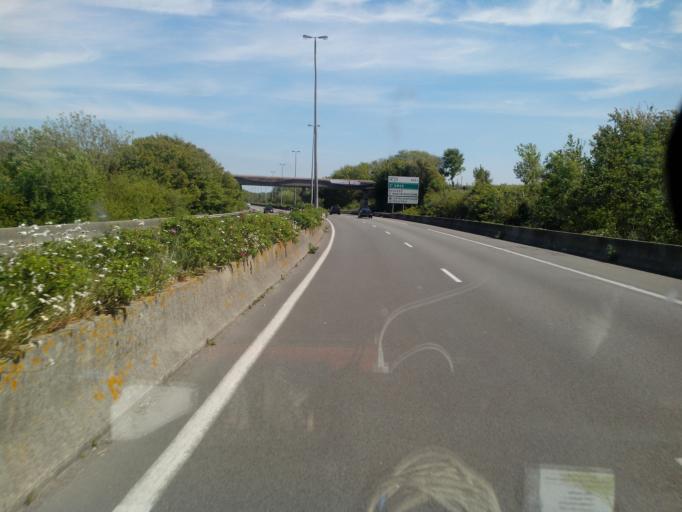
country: FR
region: Nord-Pas-de-Calais
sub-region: Departement du Pas-de-Calais
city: Saint-Martin-Boulogne
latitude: 50.7372
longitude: 1.6329
